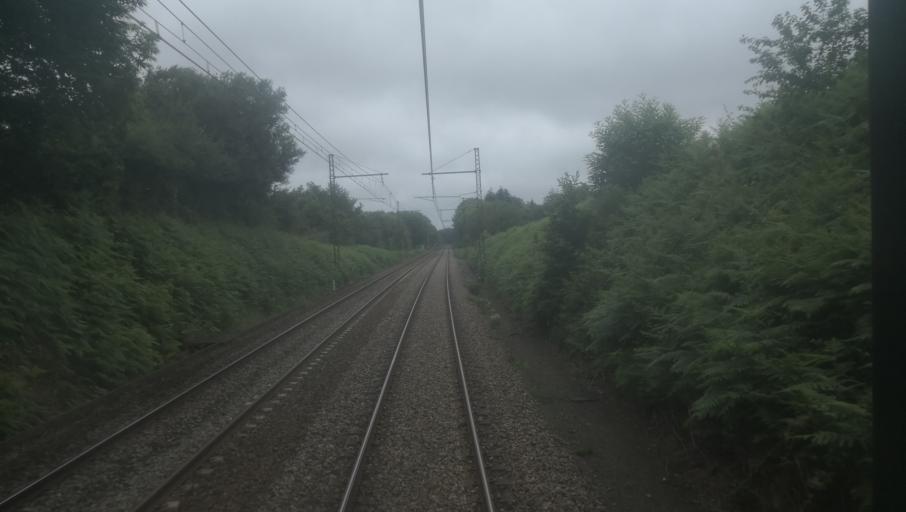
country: FR
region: Limousin
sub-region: Departement de la Creuse
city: La Souterraine
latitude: 46.2645
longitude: 1.4739
